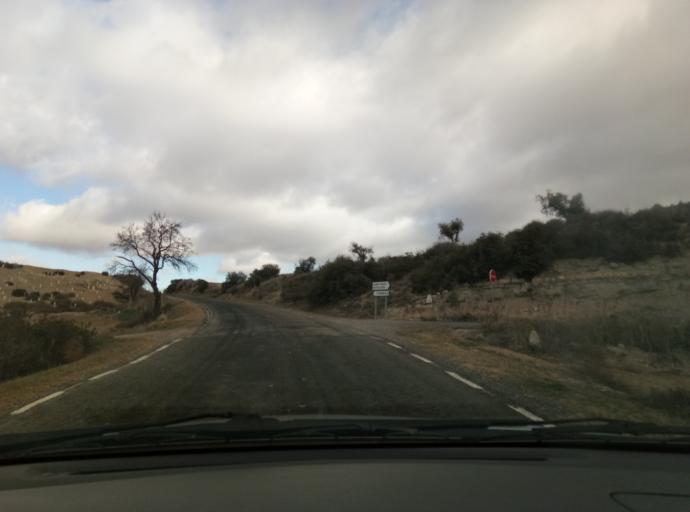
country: ES
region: Catalonia
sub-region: Provincia de Lleida
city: Nalec
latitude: 41.5876
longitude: 1.0850
